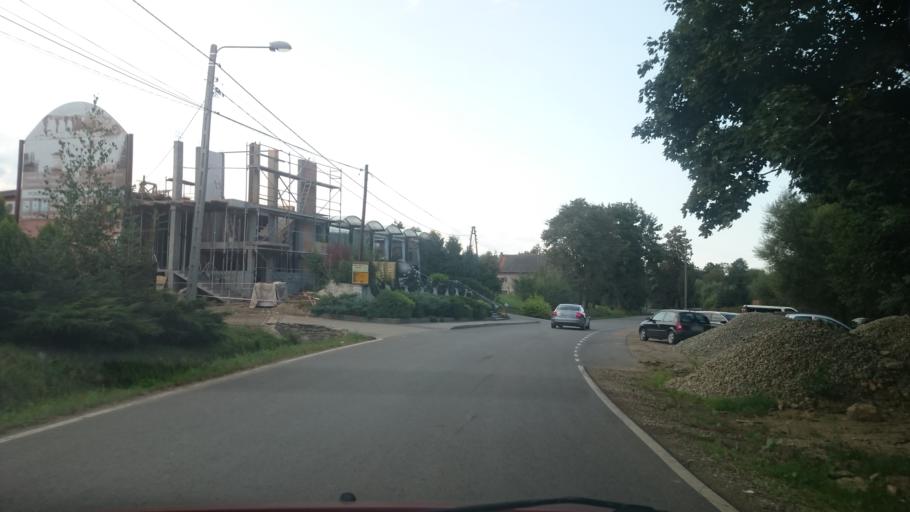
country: PL
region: Lower Silesian Voivodeship
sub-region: Powiat zabkowicki
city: Ziebice
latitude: 50.5575
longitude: 17.0526
